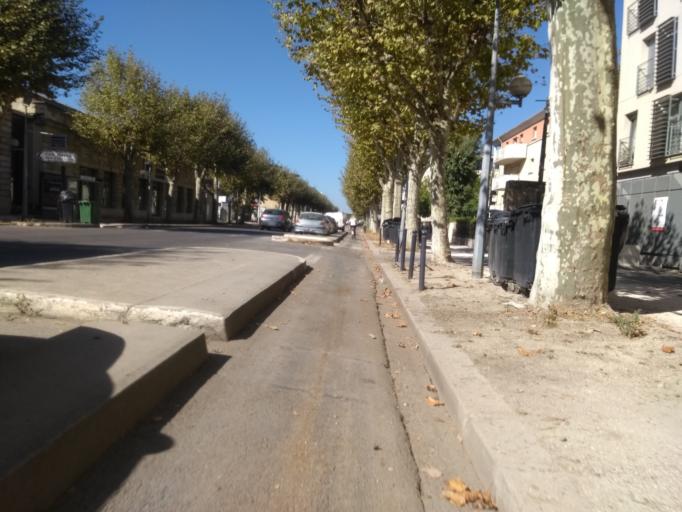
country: FR
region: Aquitaine
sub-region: Departement de la Gironde
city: Le Bouscat
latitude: 44.8633
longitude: -0.5726
